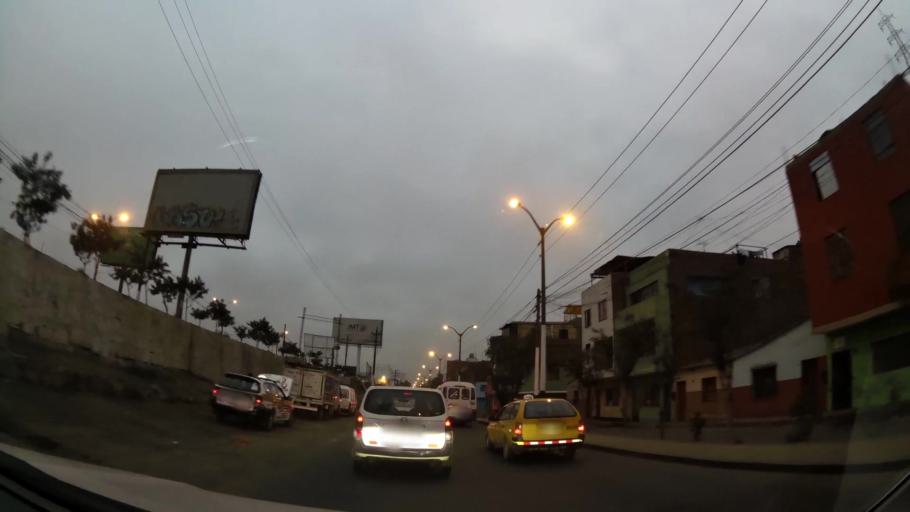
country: PE
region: Lima
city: Lima
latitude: -12.0377
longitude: -77.0147
